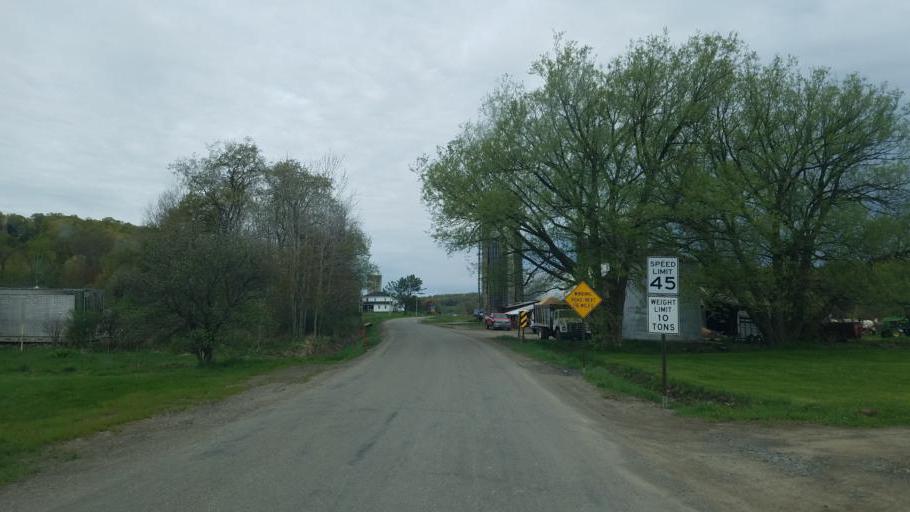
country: US
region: Pennsylvania
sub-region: Tioga County
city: Westfield
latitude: 41.9194
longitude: -77.7492
